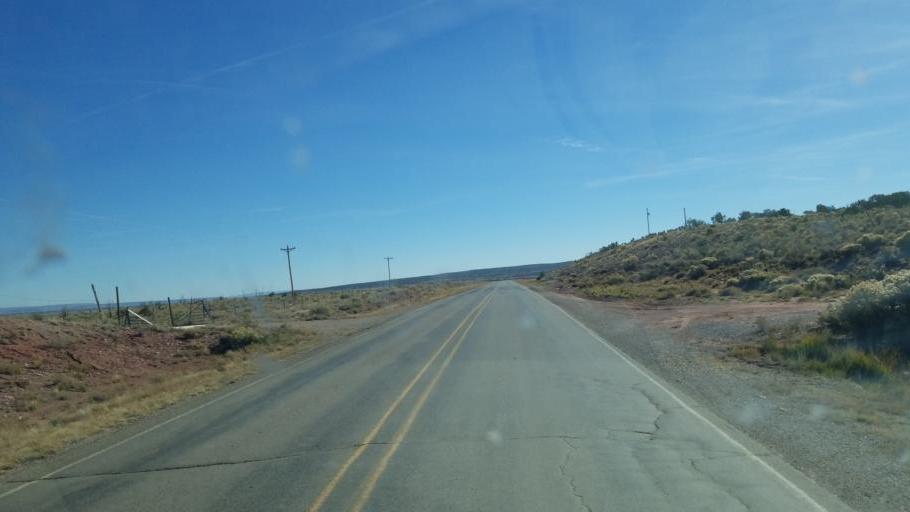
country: US
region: New Mexico
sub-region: McKinley County
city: Thoreau
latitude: 35.3981
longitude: -108.0511
